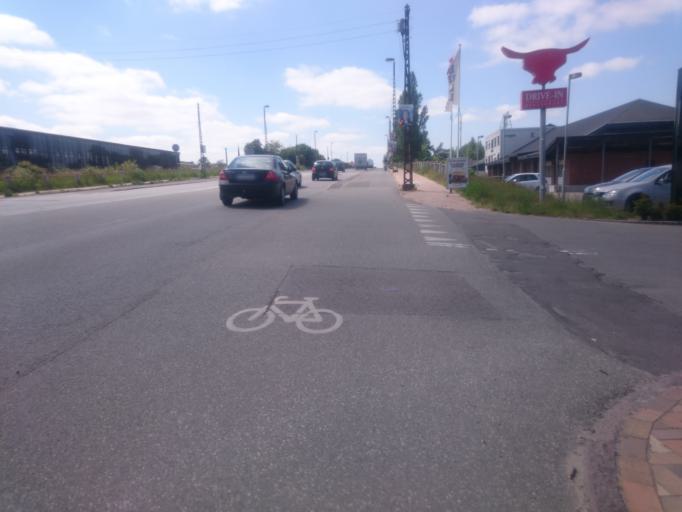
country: DK
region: South Denmark
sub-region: Odense Kommune
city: Odense
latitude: 55.3945
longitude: 10.3636
